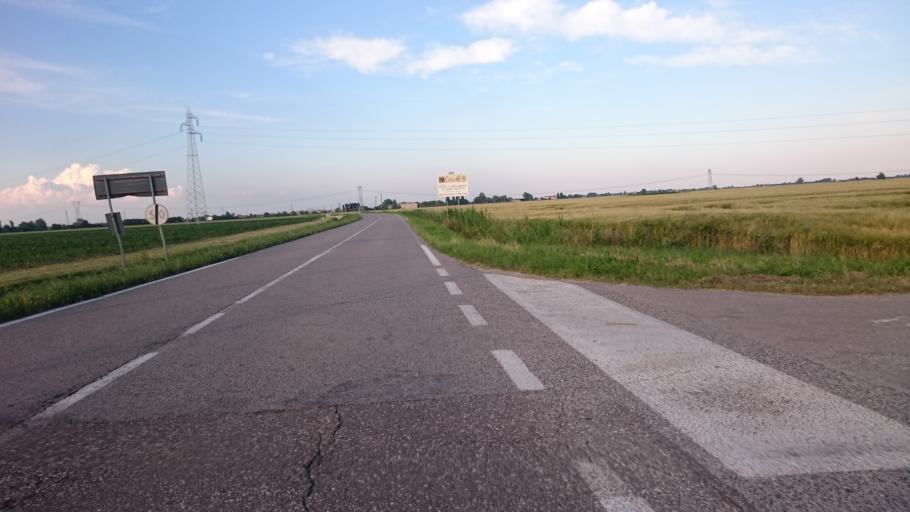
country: IT
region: Veneto
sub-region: Provincia di Verona
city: Maccacari
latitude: 45.1395
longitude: 11.1570
